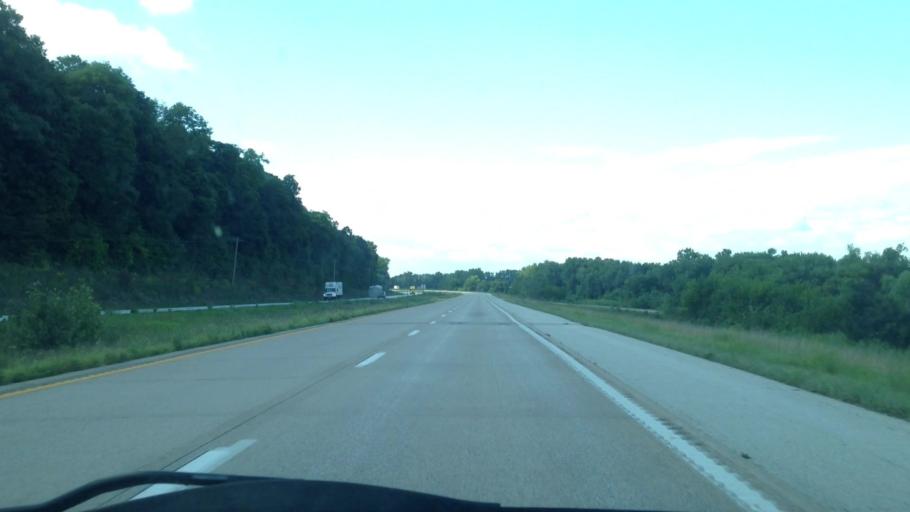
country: US
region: Missouri
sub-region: Lewis County
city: Canton
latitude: 40.2327
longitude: -91.5319
